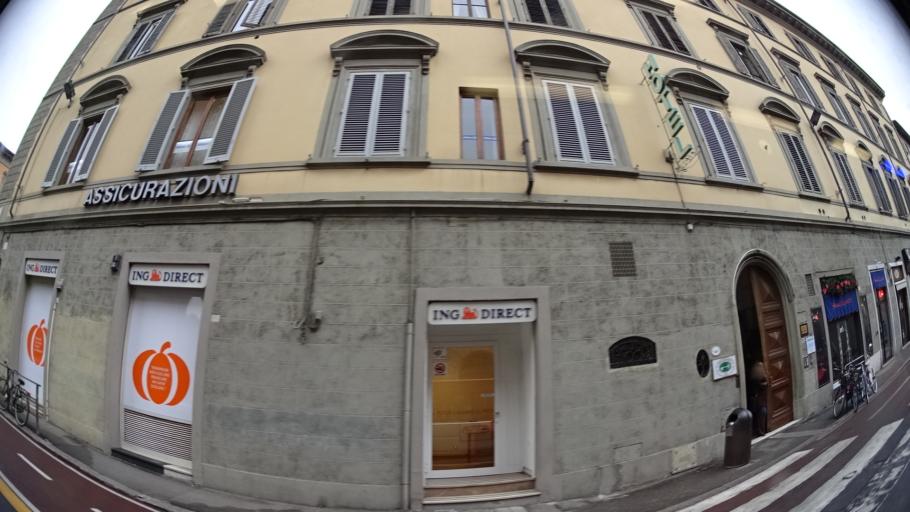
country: IT
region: Tuscany
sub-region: Province of Florence
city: Florence
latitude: 43.7845
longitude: 11.2638
